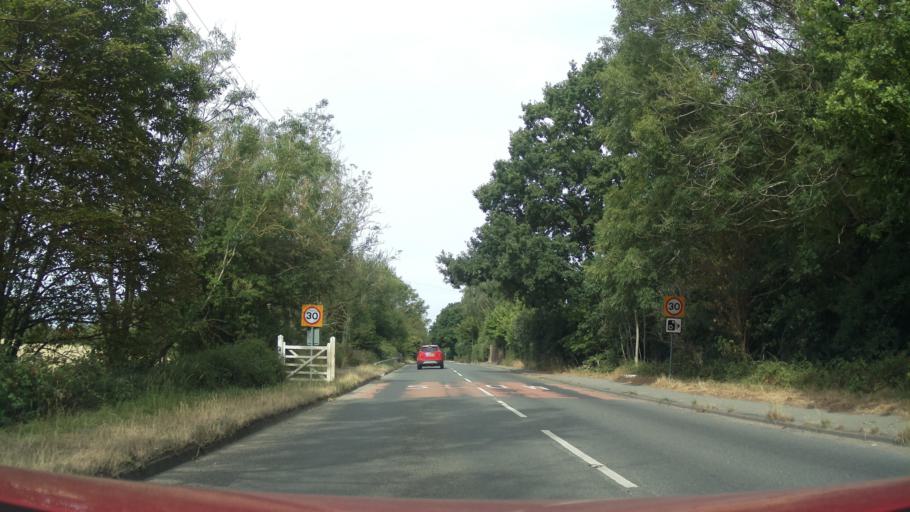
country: GB
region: England
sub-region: Surrey
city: Horley
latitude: 51.1739
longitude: -0.1430
